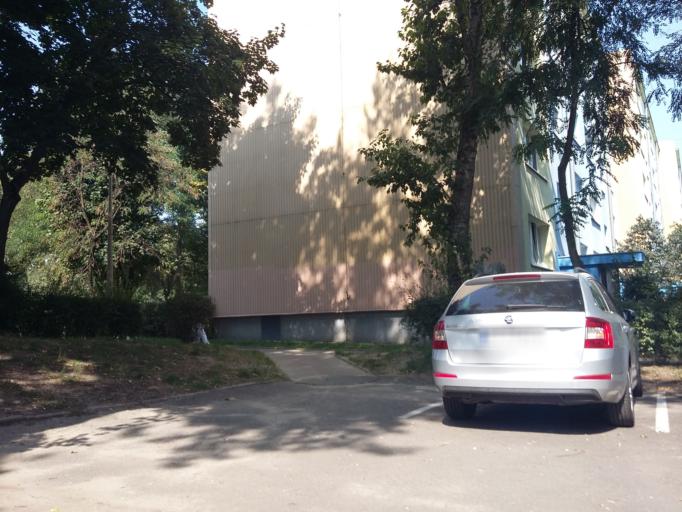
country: PL
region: Lodz Voivodeship
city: Lodz
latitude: 51.7448
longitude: 19.4151
